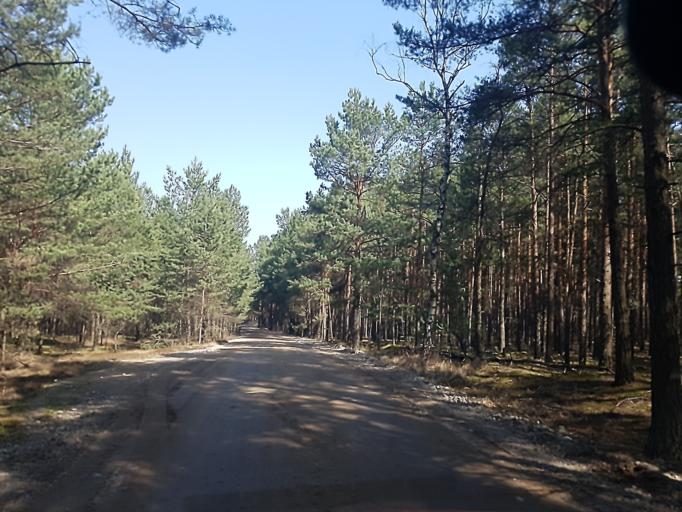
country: DE
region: Brandenburg
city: Tschernitz
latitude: 51.6629
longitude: 14.5645
